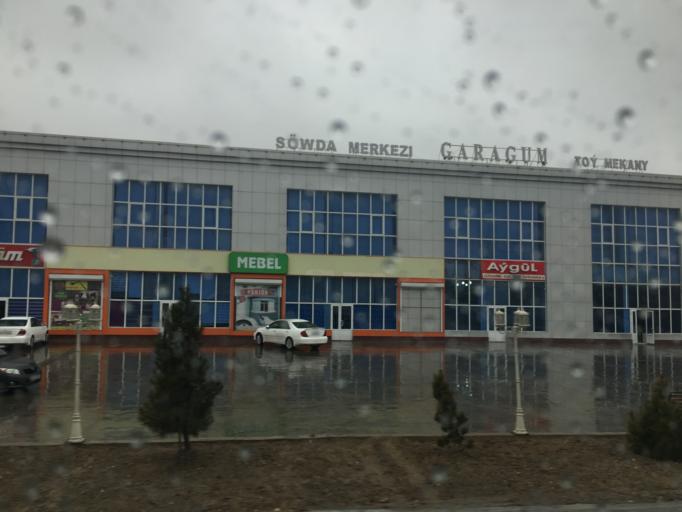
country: TM
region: Mary
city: Mary
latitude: 37.5777
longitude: 61.8350
